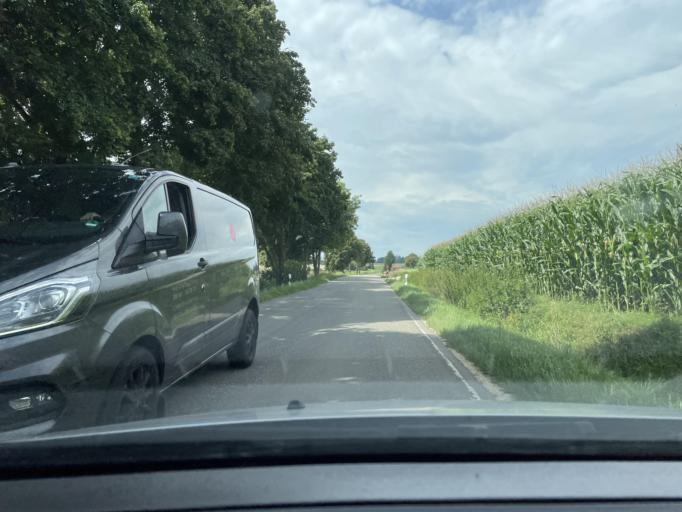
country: DE
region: Bavaria
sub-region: Lower Bavaria
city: Geisenhausen
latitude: 48.4411
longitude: 12.2654
